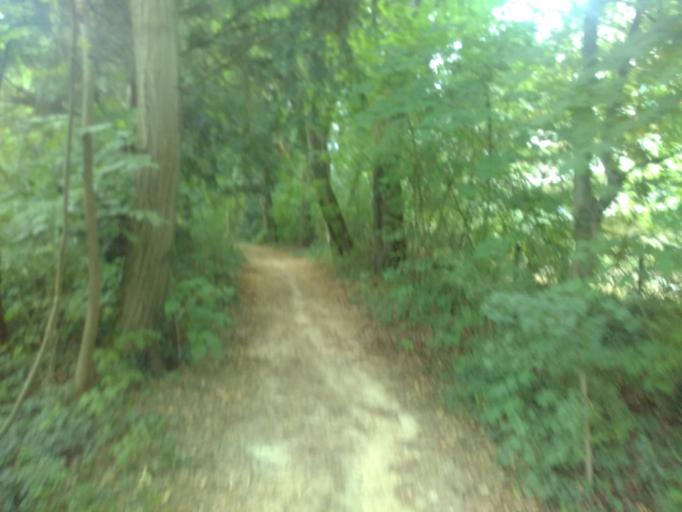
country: FR
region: Rhone-Alpes
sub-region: Departement de l'Isere
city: La Tronche
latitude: 45.2055
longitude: 5.7545
